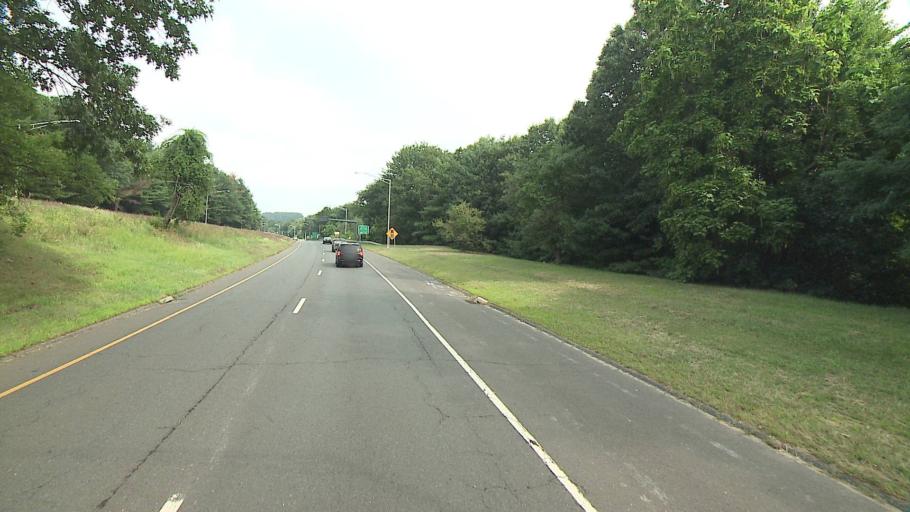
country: US
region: Connecticut
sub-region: New Haven County
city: Waterbury
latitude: 41.5684
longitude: -73.0583
